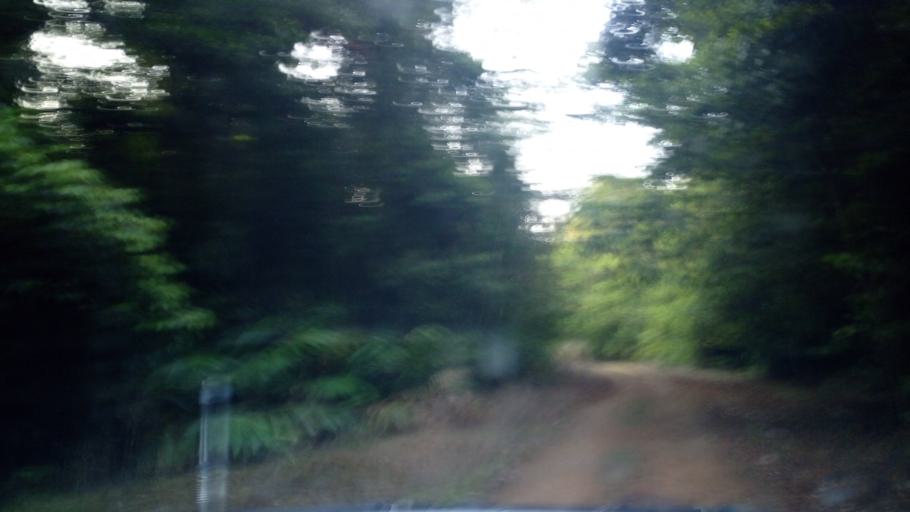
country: AU
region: Queensland
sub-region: Tablelands
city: Atherton
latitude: -17.3706
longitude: 145.7539
